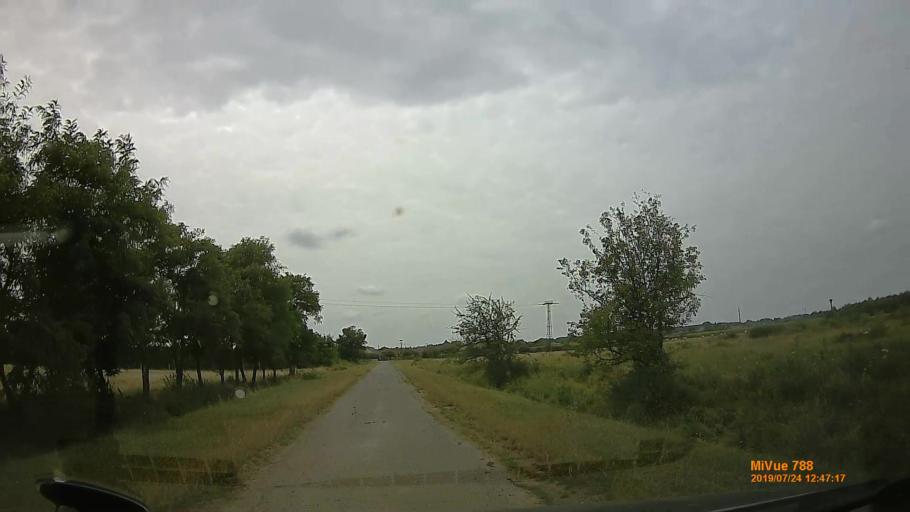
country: HU
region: Szabolcs-Szatmar-Bereg
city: Aranyosapati
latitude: 48.1943
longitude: 22.3182
